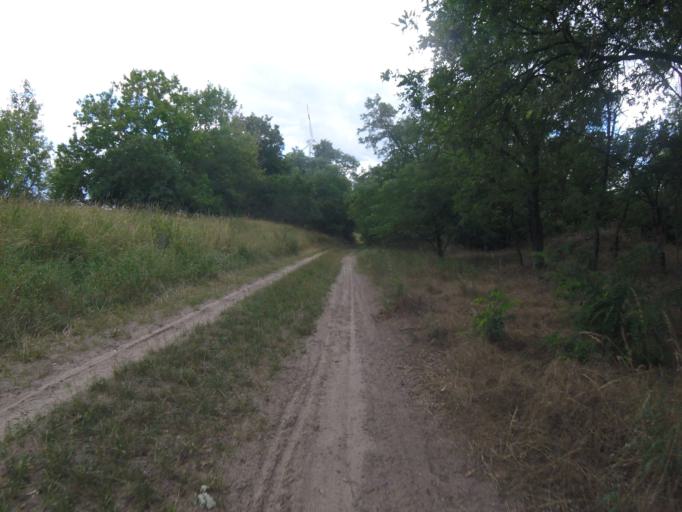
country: DE
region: Brandenburg
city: Mittenwalde
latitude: 52.2560
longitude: 13.5842
